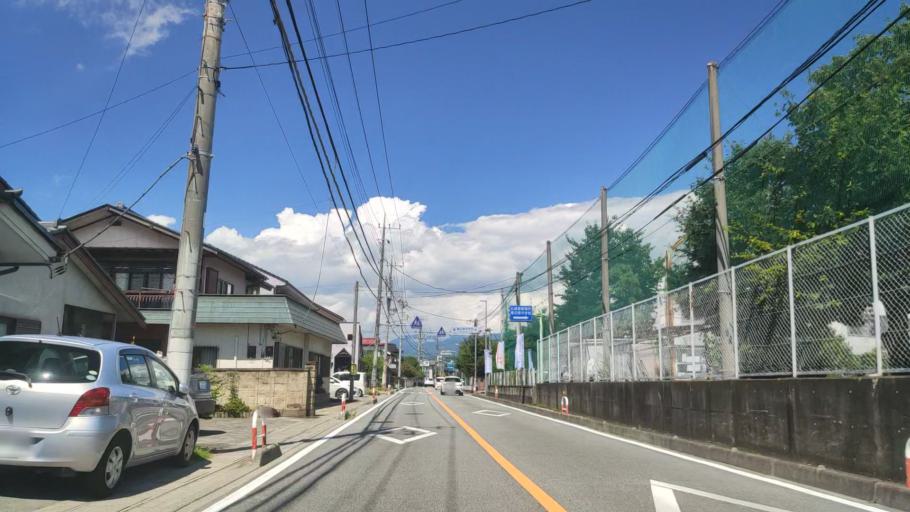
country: JP
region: Yamanashi
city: Isawa
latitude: 35.6638
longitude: 138.6427
